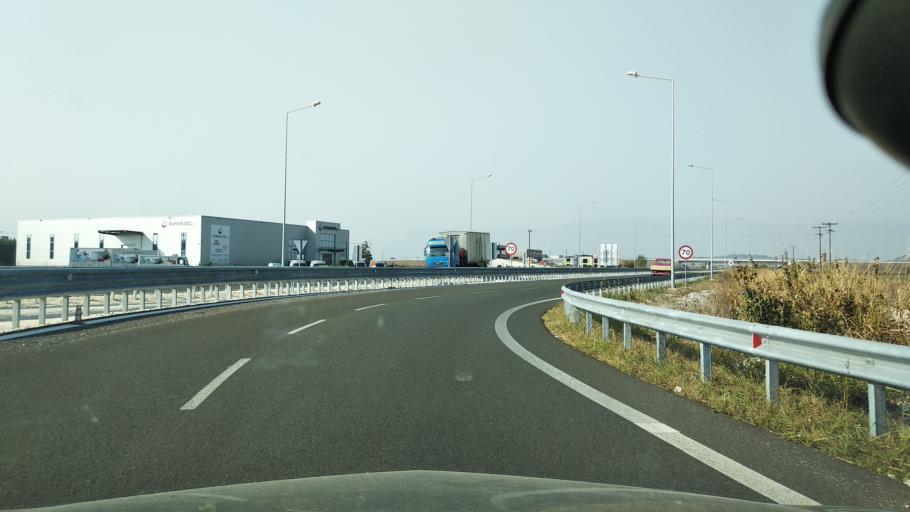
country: GR
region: Thessaly
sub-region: Trikala
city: Megalochori
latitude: 39.5668
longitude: 21.8211
